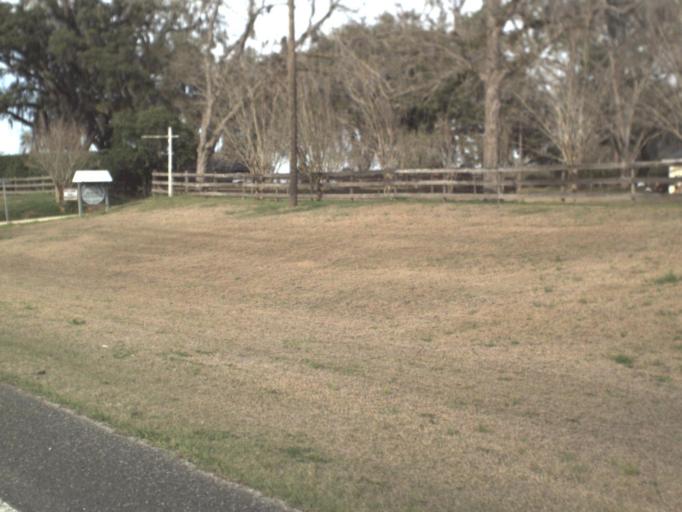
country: US
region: Florida
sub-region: Jefferson County
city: Monticello
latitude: 30.6184
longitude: -83.8722
